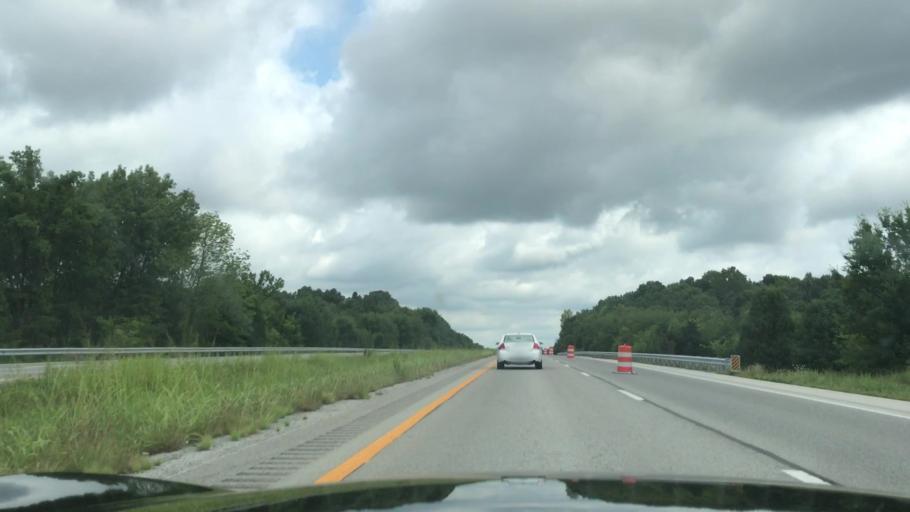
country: US
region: Kentucky
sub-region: Butler County
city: Morgantown
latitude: 37.1106
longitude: -86.6408
